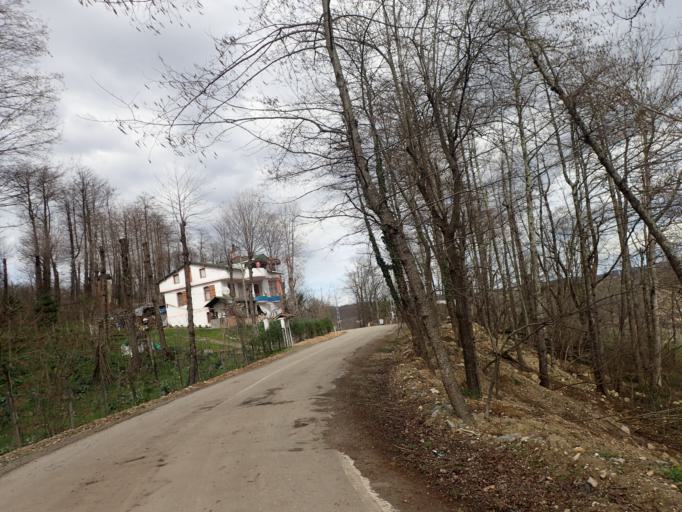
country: TR
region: Ordu
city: Kumru
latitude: 40.9385
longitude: 37.2624
